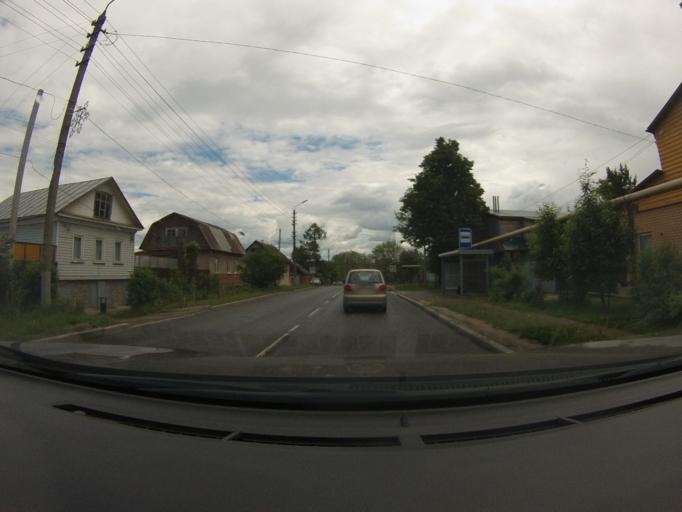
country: RU
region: Tula
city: Gorelki
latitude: 54.2385
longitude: 37.6437
